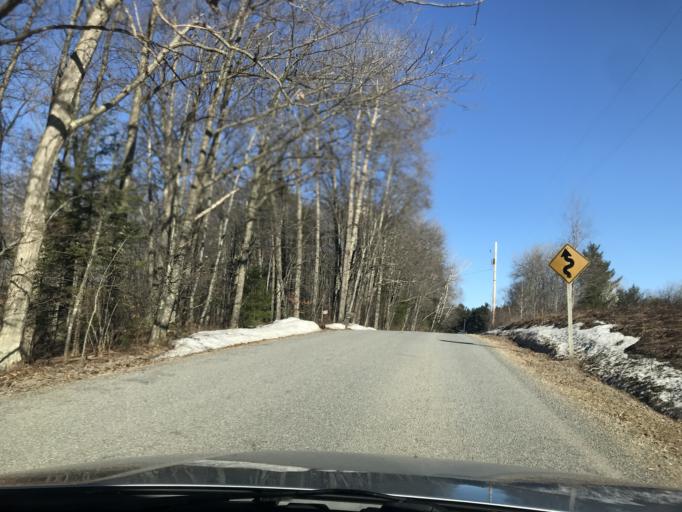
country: US
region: Wisconsin
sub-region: Marinette County
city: Niagara
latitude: 45.3869
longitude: -88.0448
